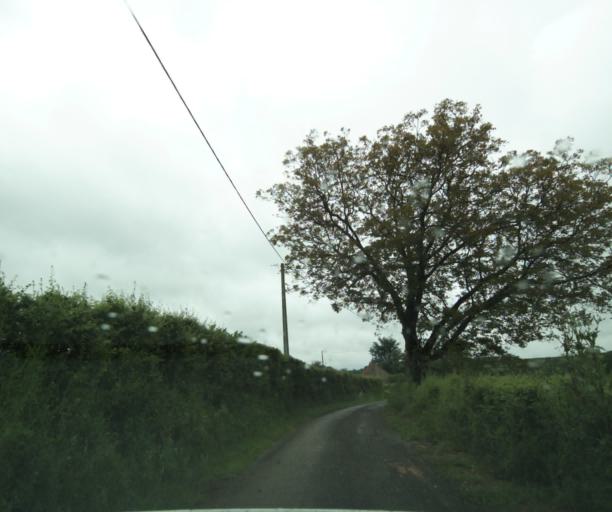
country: FR
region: Bourgogne
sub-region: Departement de Saone-et-Loire
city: Charolles
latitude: 46.4930
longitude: 4.3549
